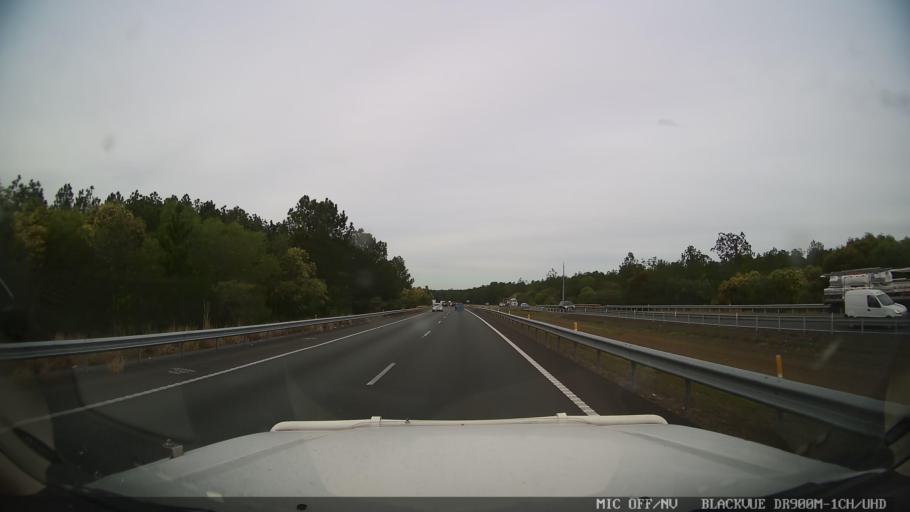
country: AU
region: Queensland
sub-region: Moreton Bay
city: Caboolture
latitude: -26.9848
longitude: 152.9798
